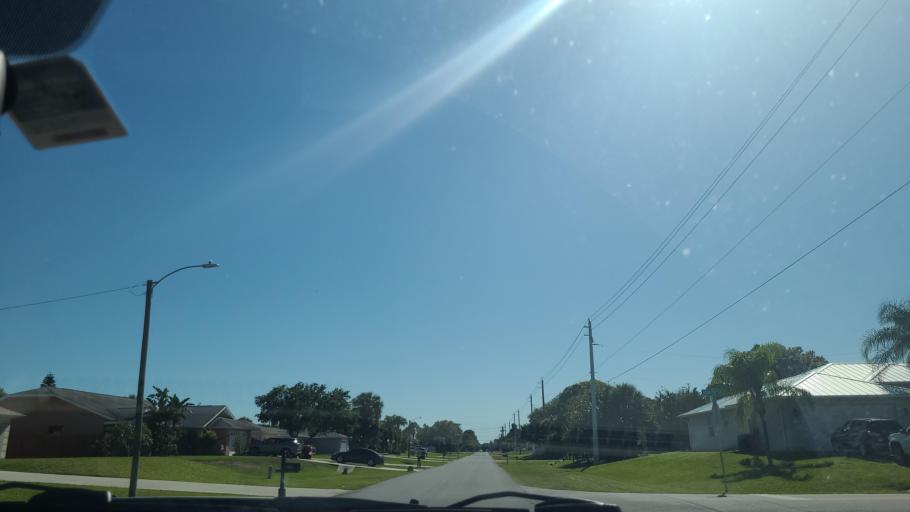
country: US
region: Florida
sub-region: Indian River County
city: Sebastian
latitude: 27.7799
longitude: -80.4829
